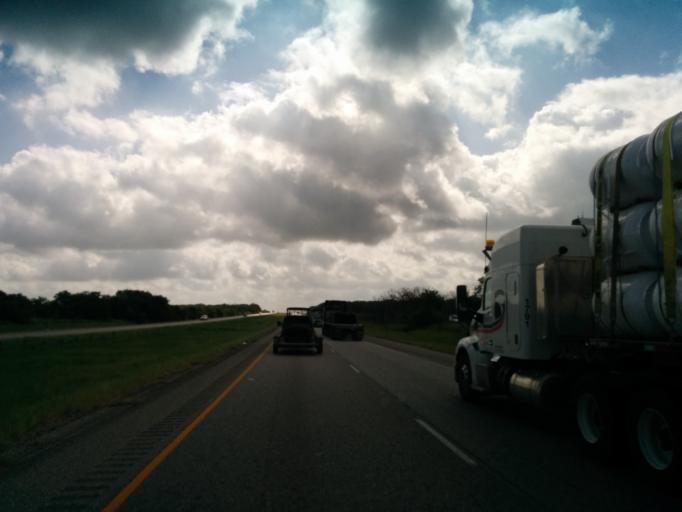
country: US
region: Texas
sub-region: Gonzales County
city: Waelder
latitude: 29.6592
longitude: -97.4066
